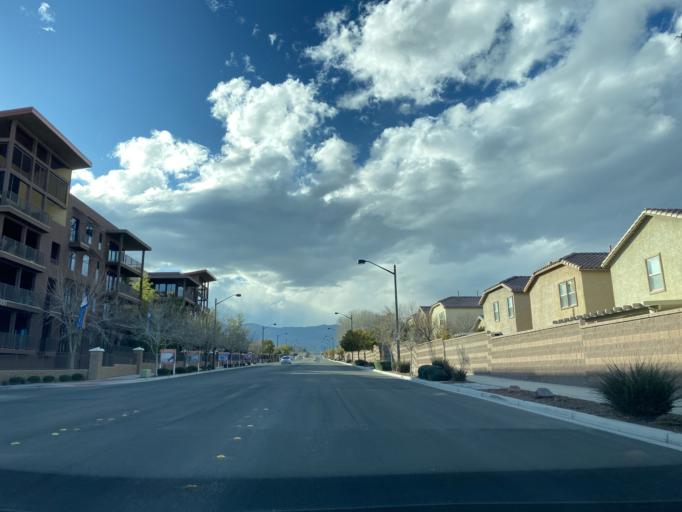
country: US
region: Nevada
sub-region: Clark County
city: Summerlin South
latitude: 36.2828
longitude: -115.2933
